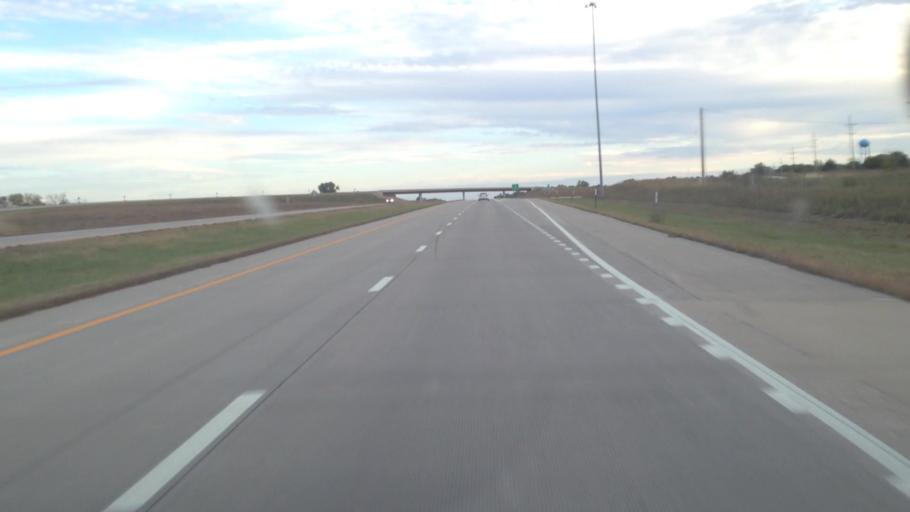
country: US
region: Kansas
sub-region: Franklin County
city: Ottawa
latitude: 38.6924
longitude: -95.2673
